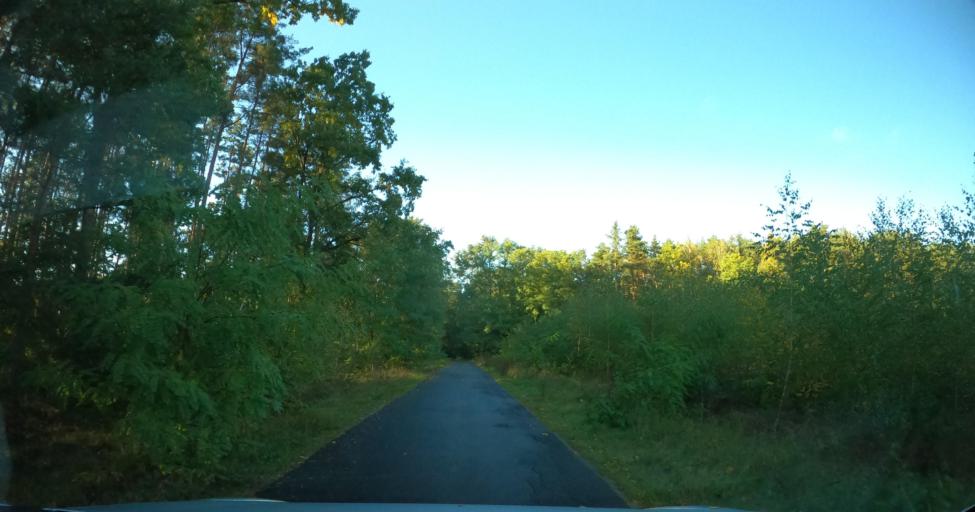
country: PL
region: Lubusz
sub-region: Powiat zielonogorski
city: Zabor
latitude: 51.9642
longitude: 15.6872
